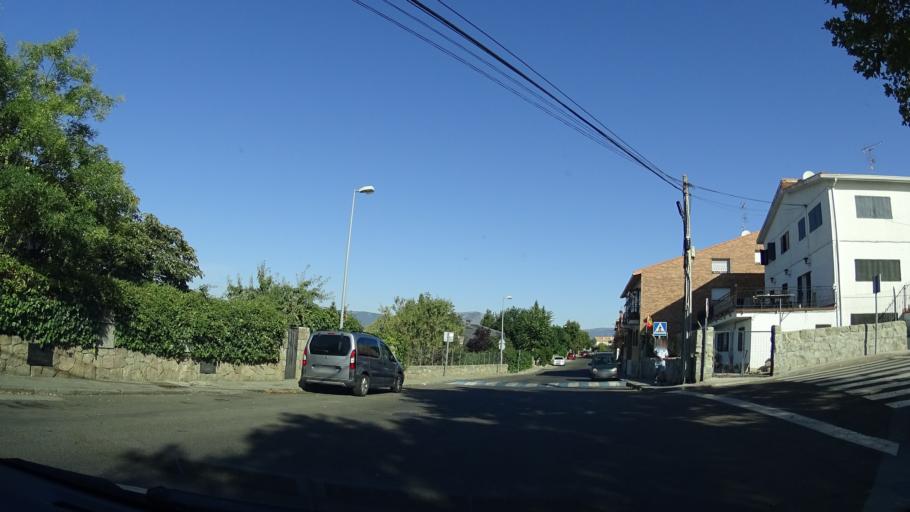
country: ES
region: Madrid
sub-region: Provincia de Madrid
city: Colmenarejo
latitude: 40.5566
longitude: -4.0158
